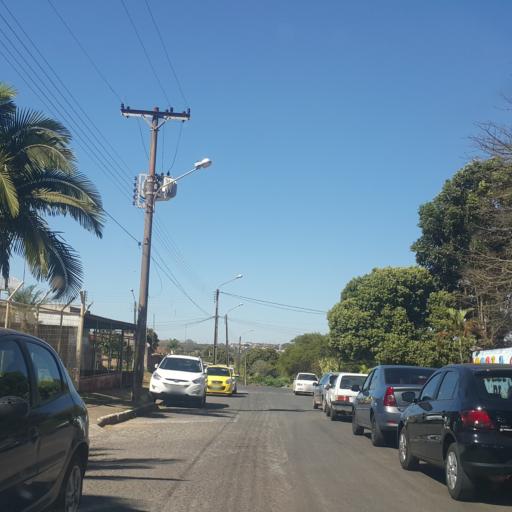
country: BR
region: Federal District
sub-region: Brasilia
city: Brasilia
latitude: -15.8247
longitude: -48.0677
